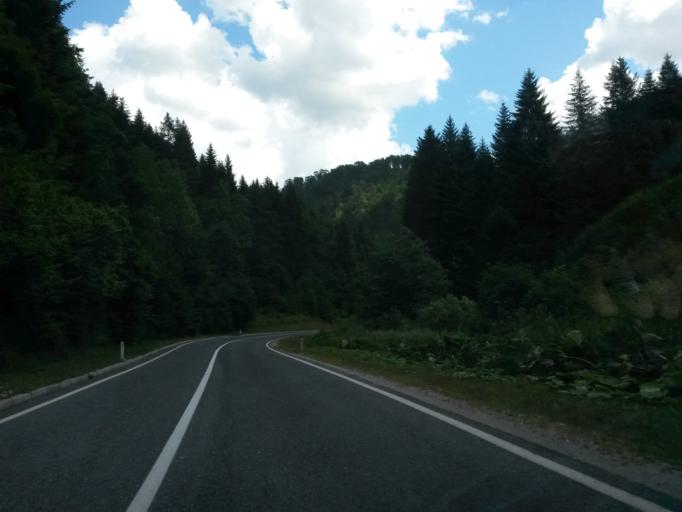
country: BA
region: Federation of Bosnia and Herzegovina
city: Bugojno
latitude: 44.0265
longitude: 17.3654
